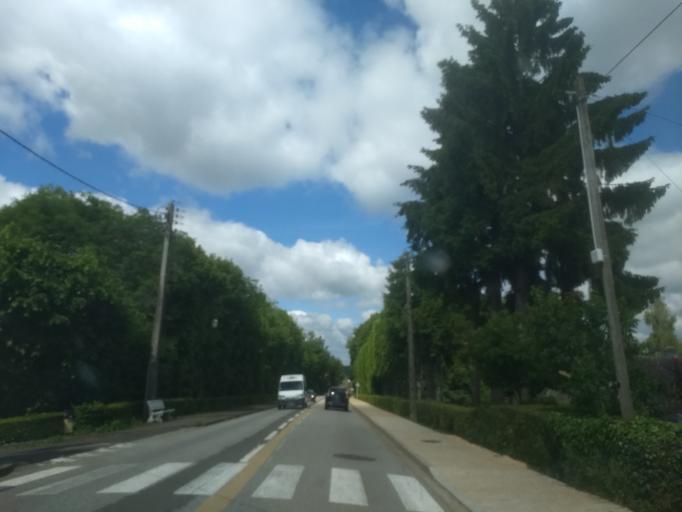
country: FR
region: Lower Normandy
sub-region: Departement de l'Orne
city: Belleme
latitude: 48.3757
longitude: 0.5587
